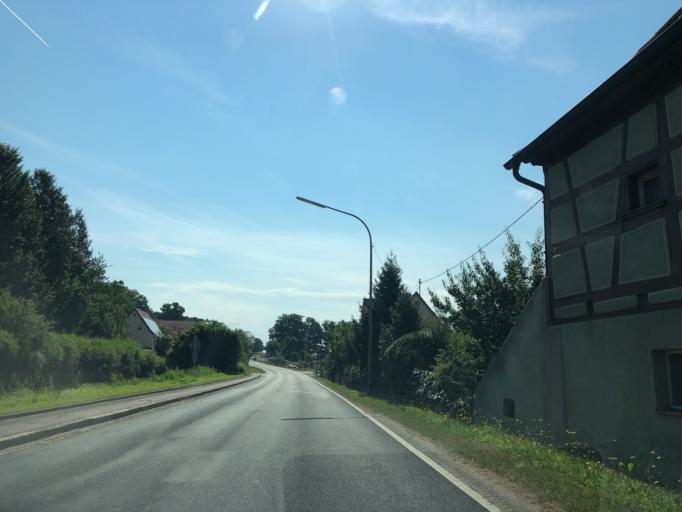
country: DE
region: Bavaria
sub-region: Regierungsbezirk Unterfranken
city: Geiselwind
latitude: 49.7689
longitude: 10.5275
